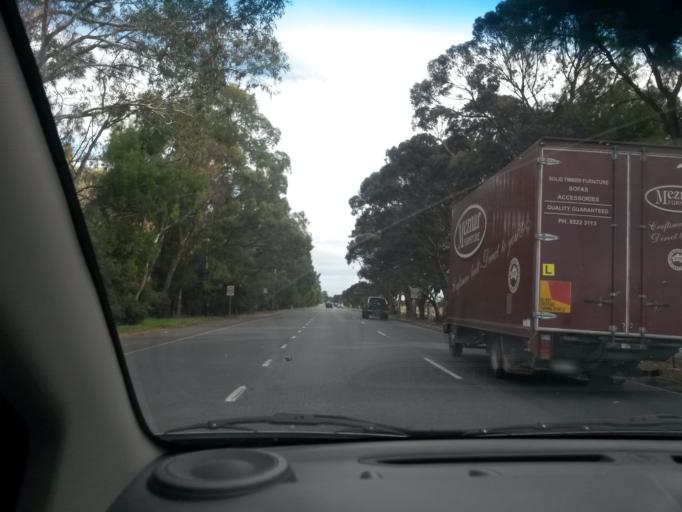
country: AU
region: South Australia
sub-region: Salisbury
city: Ingle Farm
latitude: -34.8011
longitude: 138.6388
